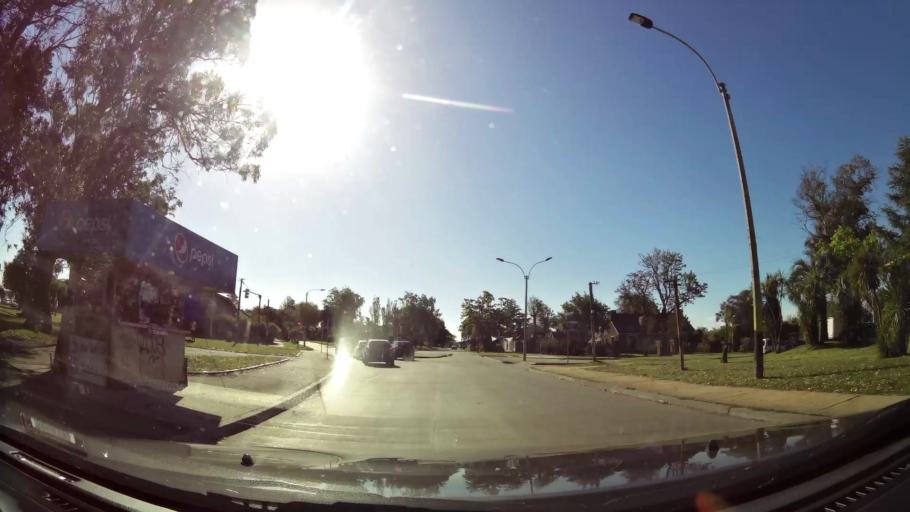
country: UY
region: Canelones
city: Paso de Carrasco
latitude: -34.8909
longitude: -56.0727
